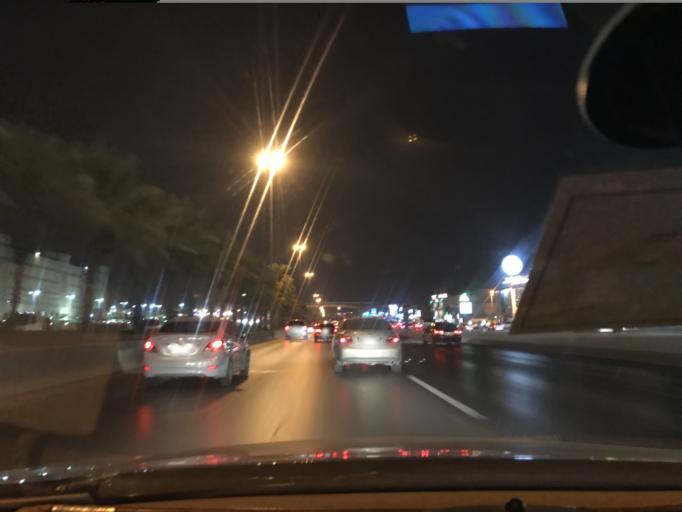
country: SA
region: Ar Riyad
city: Riyadh
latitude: 24.7556
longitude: 46.7410
